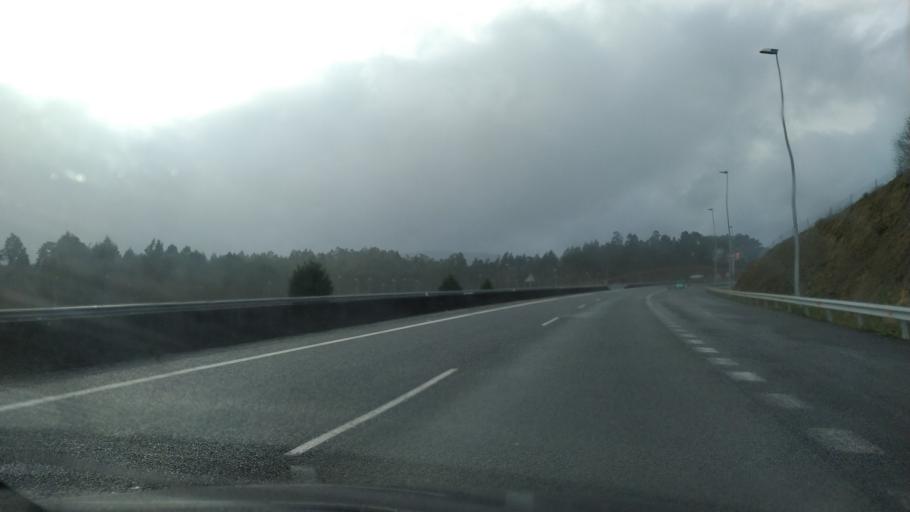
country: ES
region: Galicia
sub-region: Provincia de Pontevedra
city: Silleda
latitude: 42.7173
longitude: -8.2976
